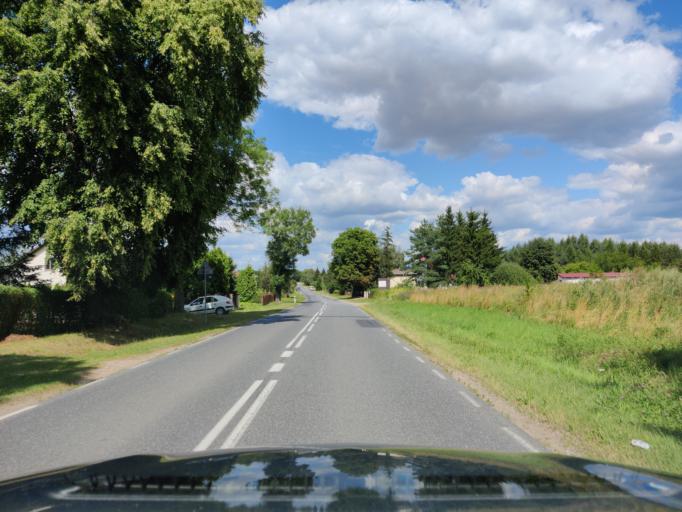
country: PL
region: Masovian Voivodeship
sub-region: Powiat wegrowski
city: Grebkow
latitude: 52.2460
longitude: 21.8921
